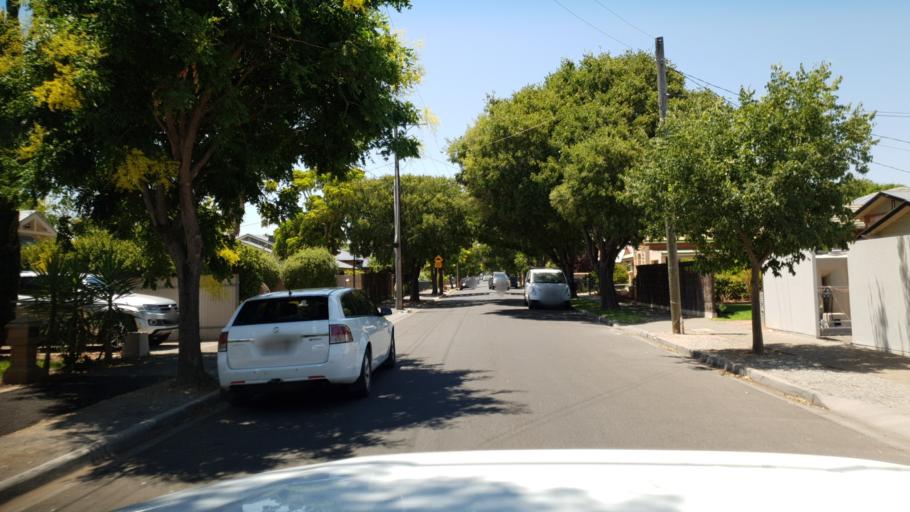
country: AU
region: South Australia
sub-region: Mitcham
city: Clarence Gardens
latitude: -34.9748
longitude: 138.5771
